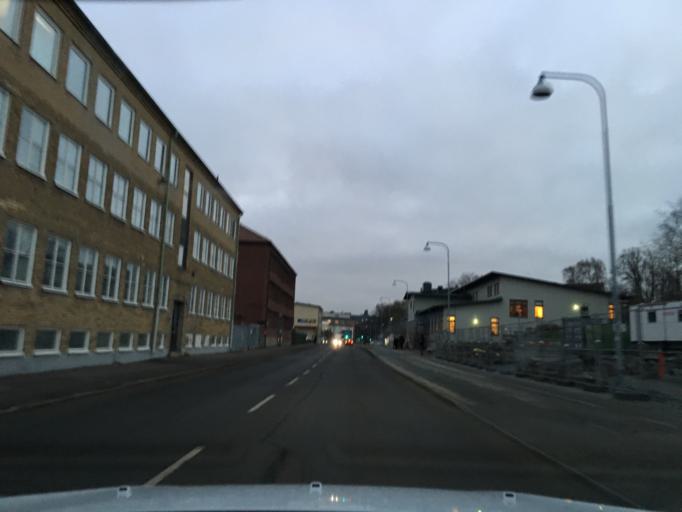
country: SE
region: Vaestra Goetaland
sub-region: Goteborg
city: Majorna
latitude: 57.7094
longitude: 11.9320
